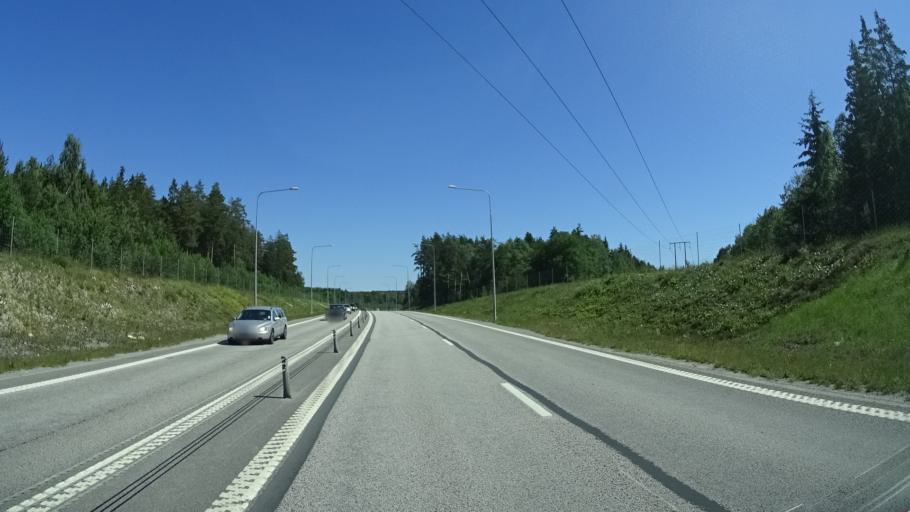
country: SE
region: Stockholm
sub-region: Taby Kommun
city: Taby
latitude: 59.4773
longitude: 18.0641
